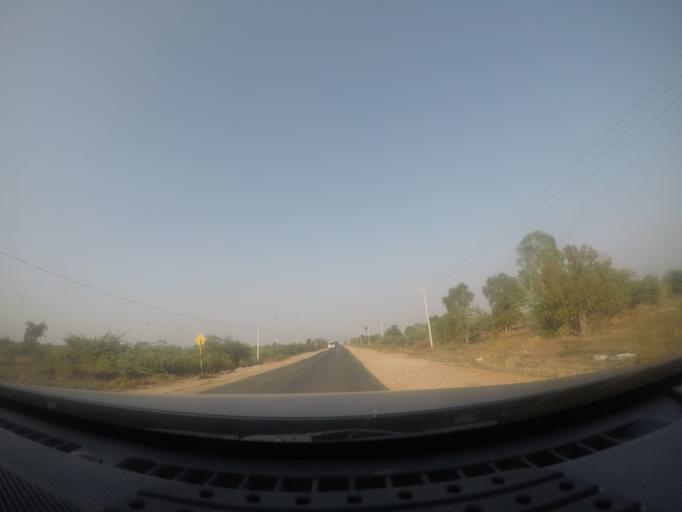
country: MM
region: Mandalay
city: Yamethin
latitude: 20.6098
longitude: 96.0706
